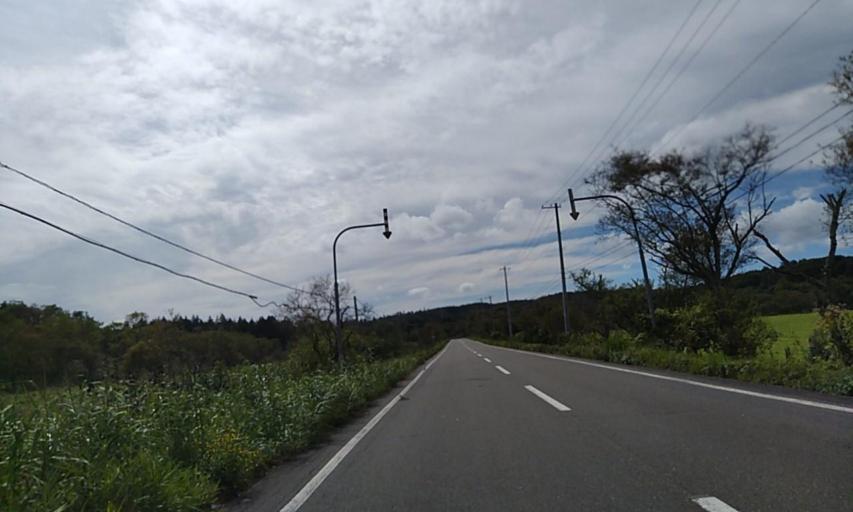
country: JP
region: Hokkaido
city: Kushiro
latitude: 42.8462
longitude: 143.8458
